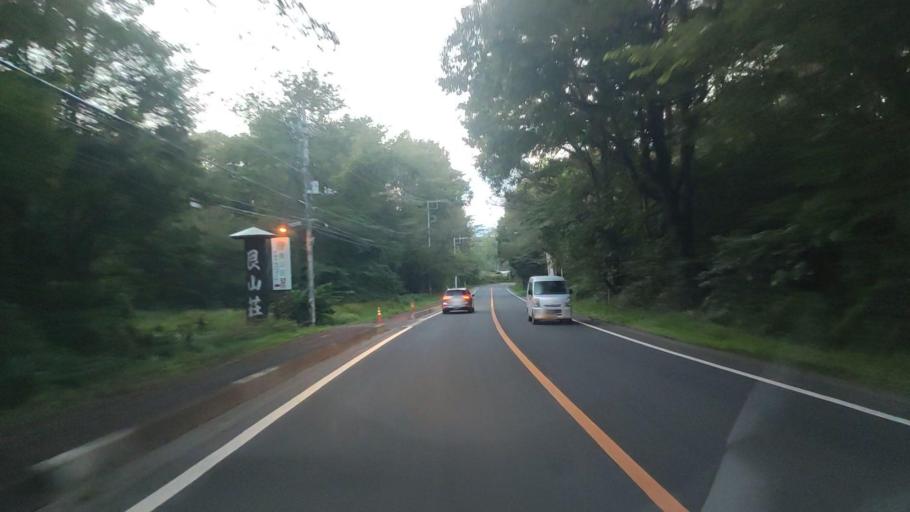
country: JP
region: Gunma
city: Nakanojomachi
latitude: 36.5194
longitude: 138.5980
